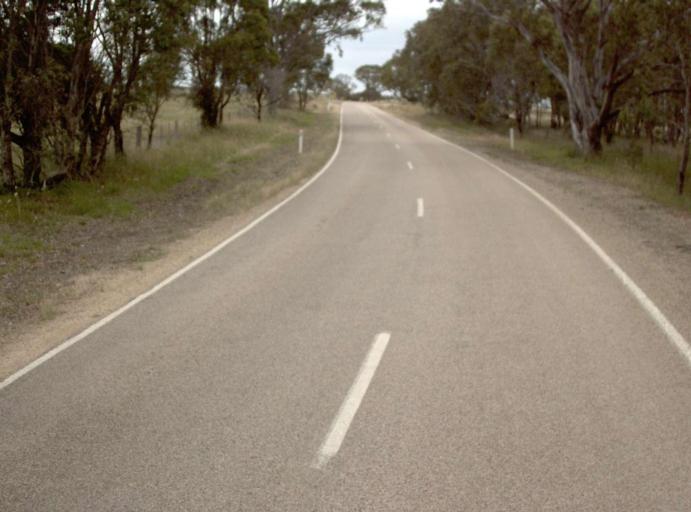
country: AU
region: Victoria
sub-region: East Gippsland
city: Bairnsdale
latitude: -37.9385
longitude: 147.5286
